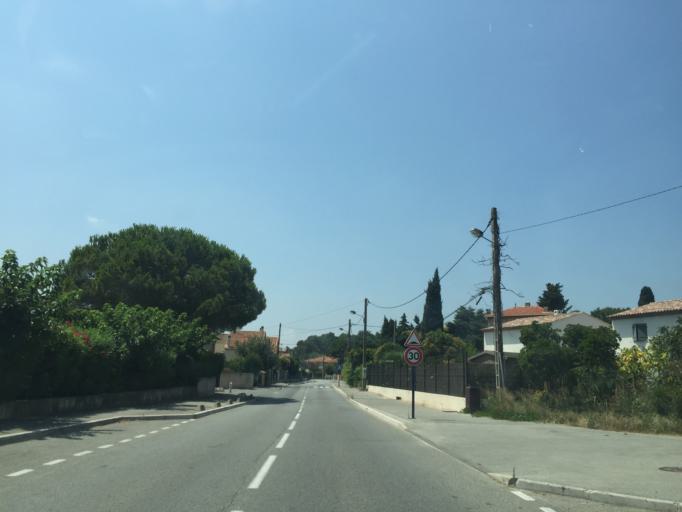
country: FR
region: Provence-Alpes-Cote d'Azur
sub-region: Departement du Var
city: Frejus
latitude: 43.4347
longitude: 6.7481
